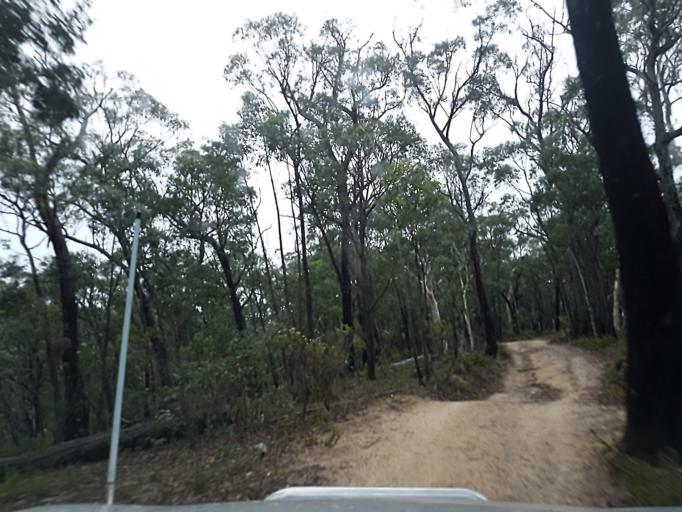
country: AU
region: New South Wales
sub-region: Snowy River
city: Jindabyne
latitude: -36.8525
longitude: 148.2282
